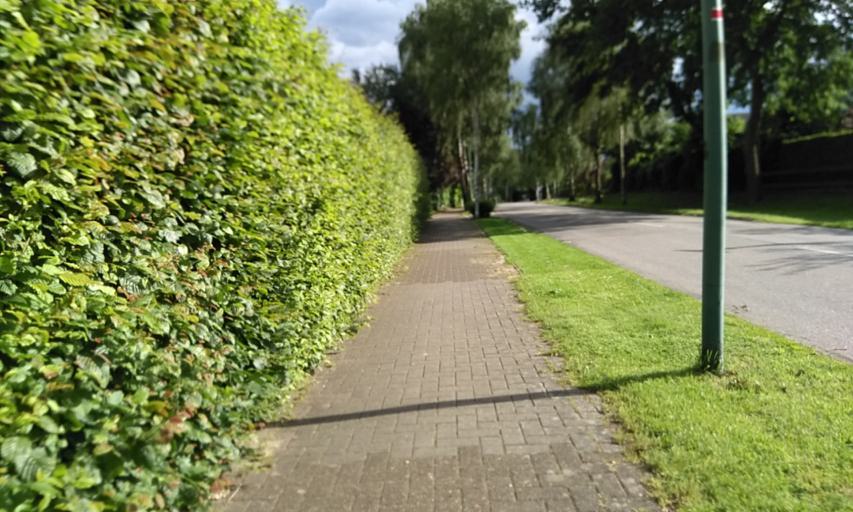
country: DE
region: Lower Saxony
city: Regesbostel
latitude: 53.4184
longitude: 9.6543
